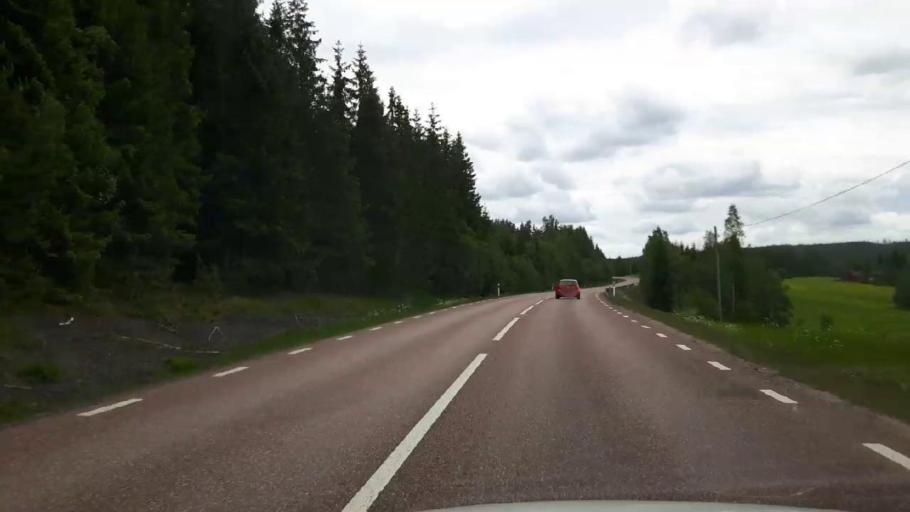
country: SE
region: Dalarna
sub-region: Hedemora Kommun
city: Brunna
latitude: 60.2248
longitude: 15.9958
